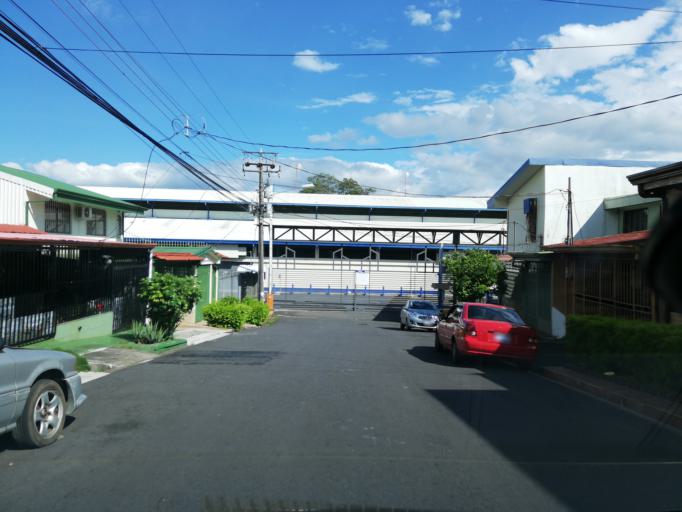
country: CR
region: Alajuela
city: Alajuela
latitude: 10.0052
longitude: -84.2075
